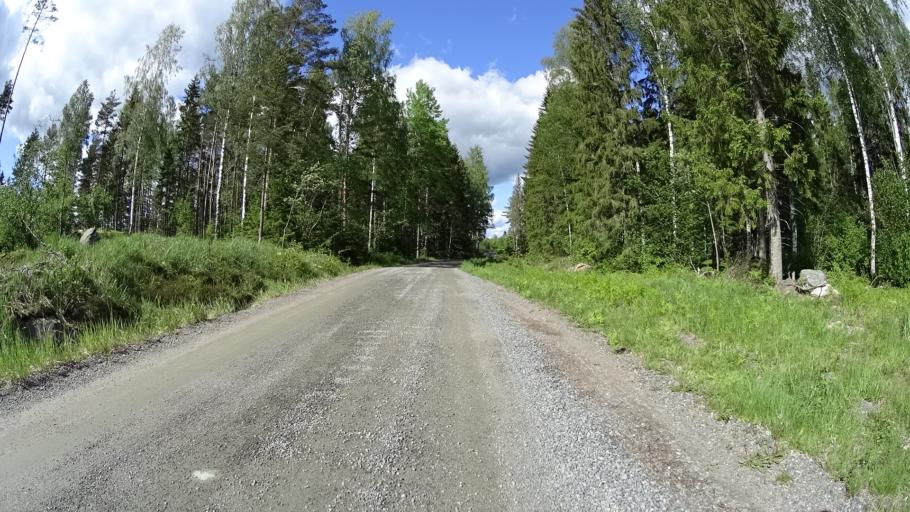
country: FI
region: Uusimaa
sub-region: Raaseporin
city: Pohja
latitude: 60.1780
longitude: 23.5874
